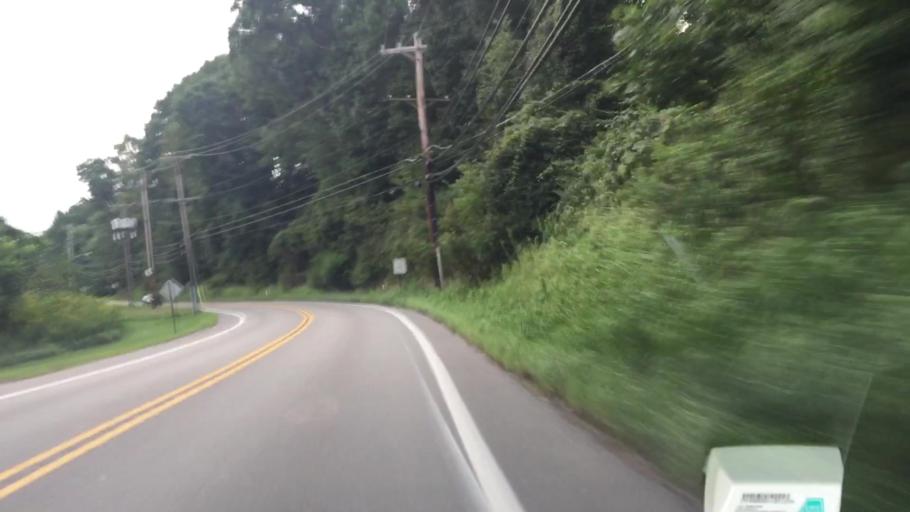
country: US
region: Pennsylvania
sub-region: Allegheny County
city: Whitehall
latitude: 40.3643
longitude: -79.9997
